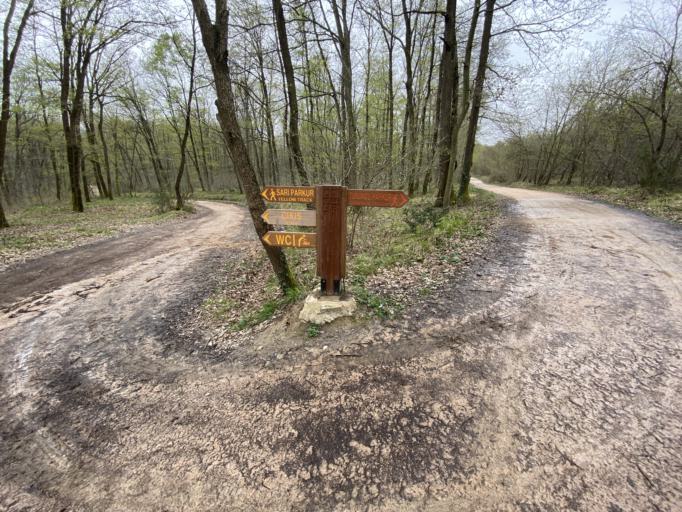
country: TR
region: Kocaeli
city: Derbent
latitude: 40.7378
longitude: 30.1690
